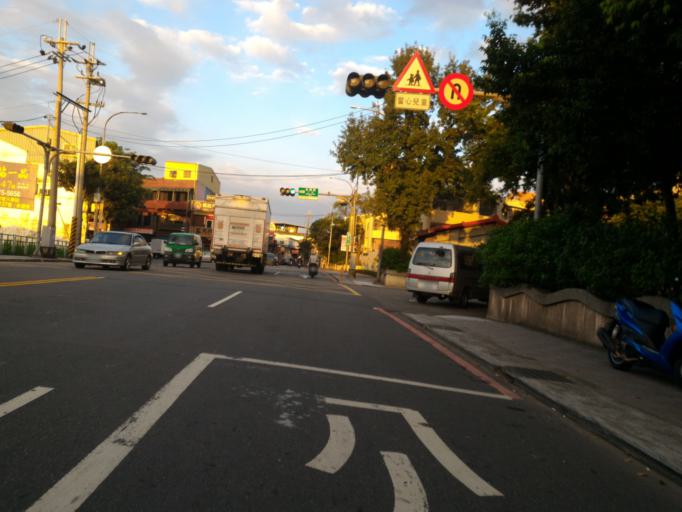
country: TW
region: Taiwan
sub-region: Taoyuan
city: Taoyuan
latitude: 24.9561
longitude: 121.3891
